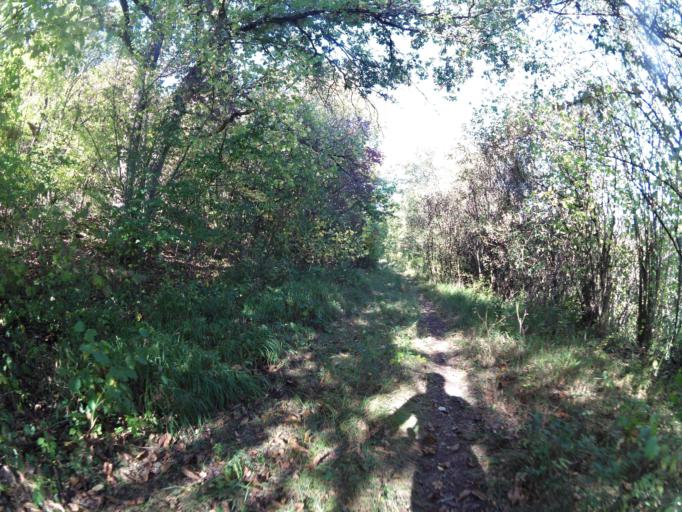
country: DE
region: Bavaria
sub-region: Regierungsbezirk Unterfranken
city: Ochsenfurt
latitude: 49.6807
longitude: 10.0471
